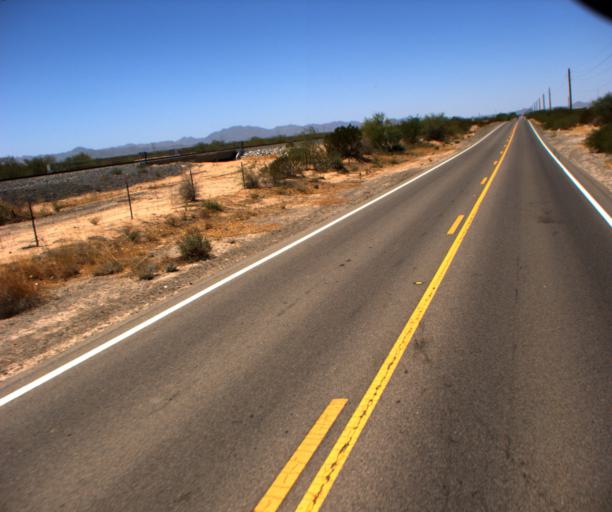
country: US
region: Arizona
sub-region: Pinal County
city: Maricopa
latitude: 33.0622
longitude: -112.2449
